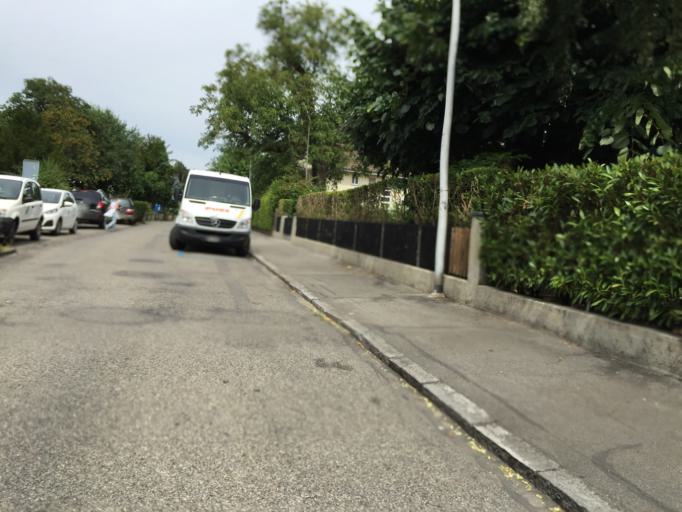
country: CH
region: Bern
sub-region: Bern-Mittelland District
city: Koniz
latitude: 46.9324
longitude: 7.4244
